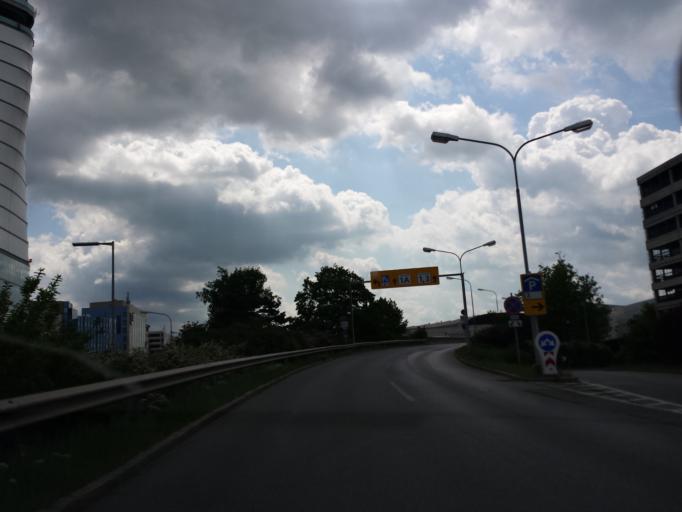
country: AT
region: Lower Austria
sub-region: Politischer Bezirk Wien-Umgebung
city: Fischamend Dorf
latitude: 48.1230
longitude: 16.5600
